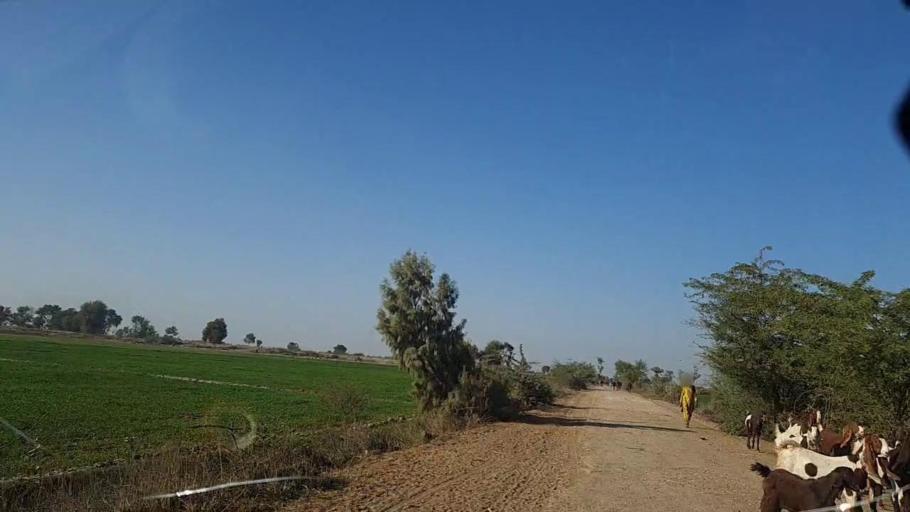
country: PK
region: Sindh
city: Khanpur
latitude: 27.7698
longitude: 69.2907
